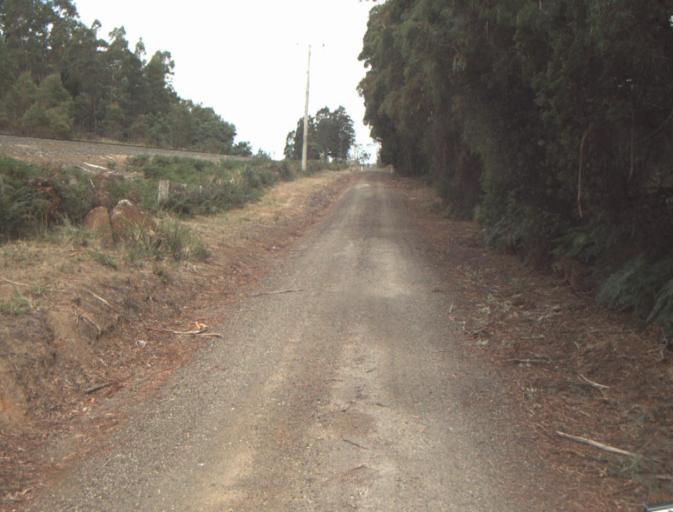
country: AU
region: Tasmania
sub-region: Launceston
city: Mayfield
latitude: -41.2778
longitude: 147.0514
